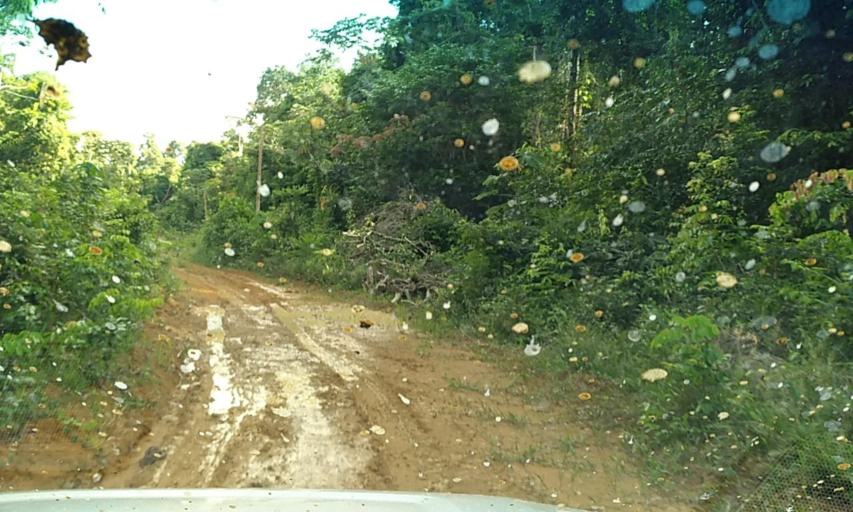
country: BR
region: Para
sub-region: Senador Jose Porfirio
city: Senador Jose Porfirio
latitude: -2.9925
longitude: -51.7439
